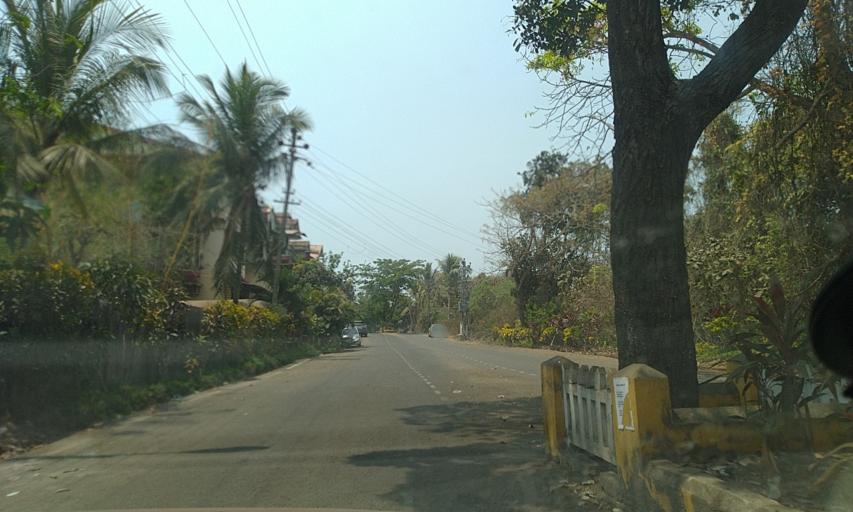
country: IN
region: Goa
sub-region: North Goa
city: Panaji
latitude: 15.5234
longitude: 73.8228
